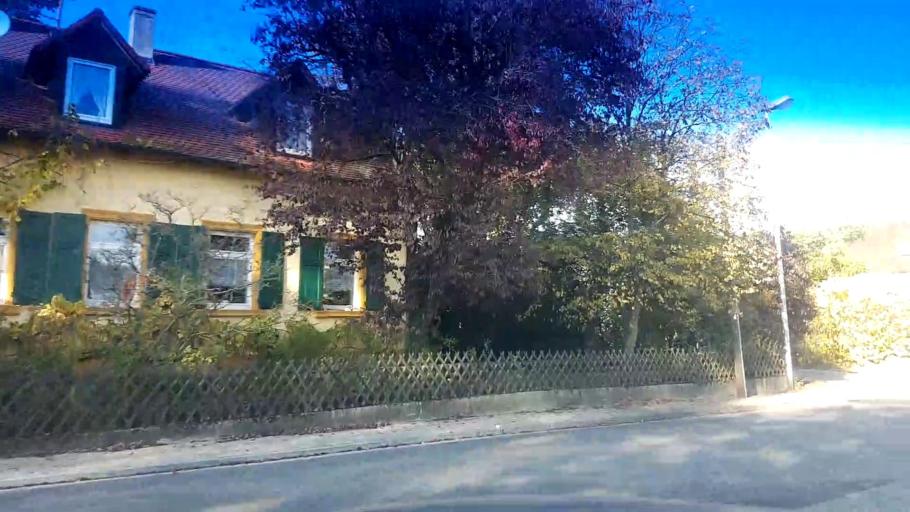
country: DE
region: Bavaria
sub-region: Upper Franconia
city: Strullendorf
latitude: 49.8654
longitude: 10.9940
